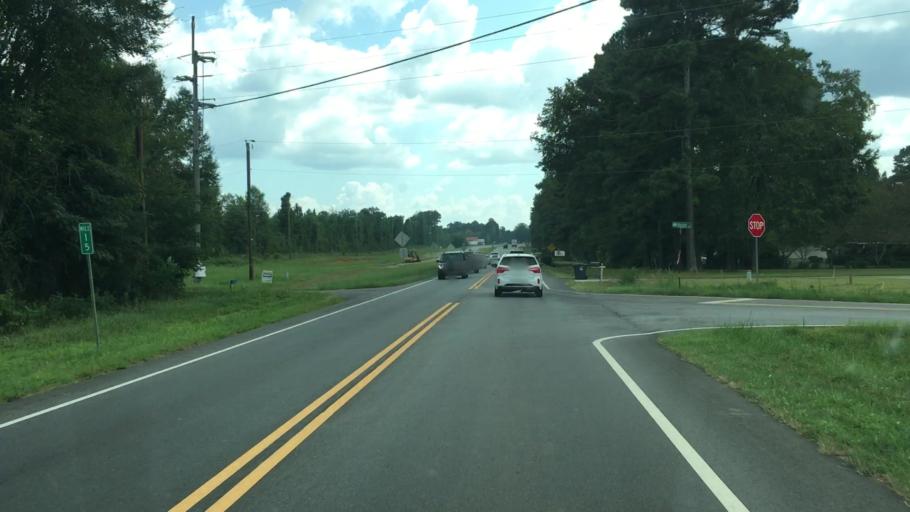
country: US
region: Georgia
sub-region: Putnam County
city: Eatonton
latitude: 33.3549
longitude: -83.3903
